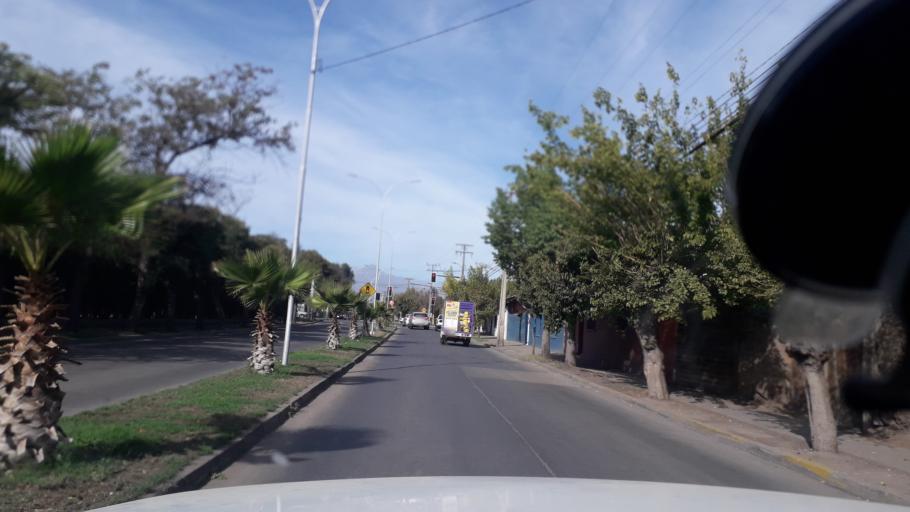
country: CL
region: Valparaiso
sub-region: Provincia de San Felipe
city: San Felipe
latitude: -32.7497
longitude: -70.7119
